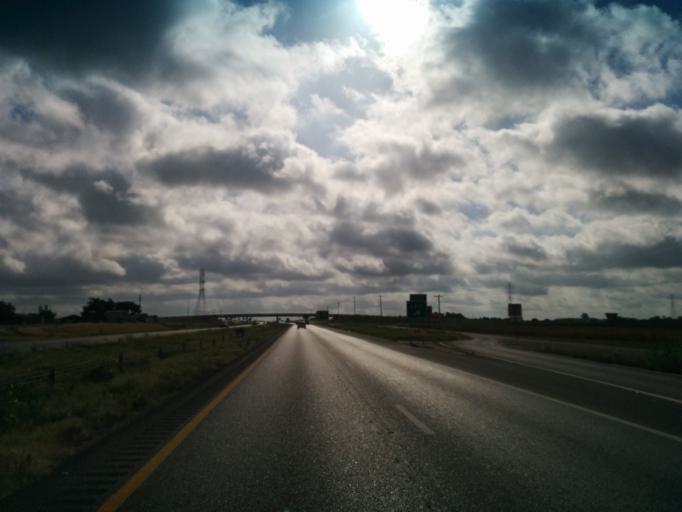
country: US
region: Texas
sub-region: Guadalupe County
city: Marion
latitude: 29.5350
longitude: -98.0894
